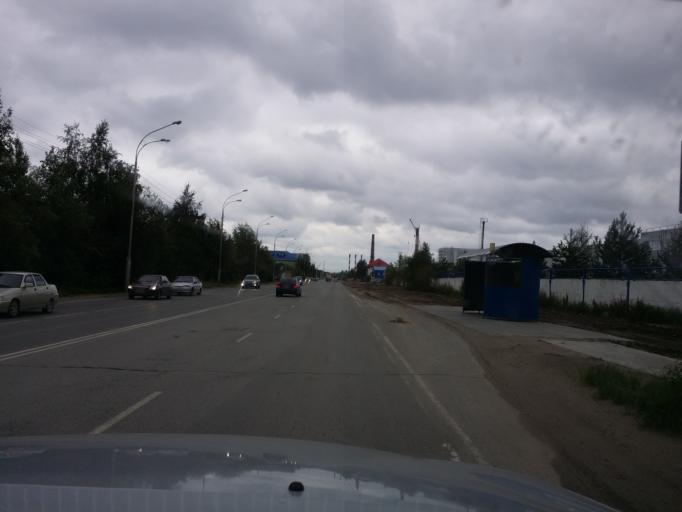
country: RU
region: Khanty-Mansiyskiy Avtonomnyy Okrug
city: Nizhnevartovsk
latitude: 60.9446
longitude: 76.5481
